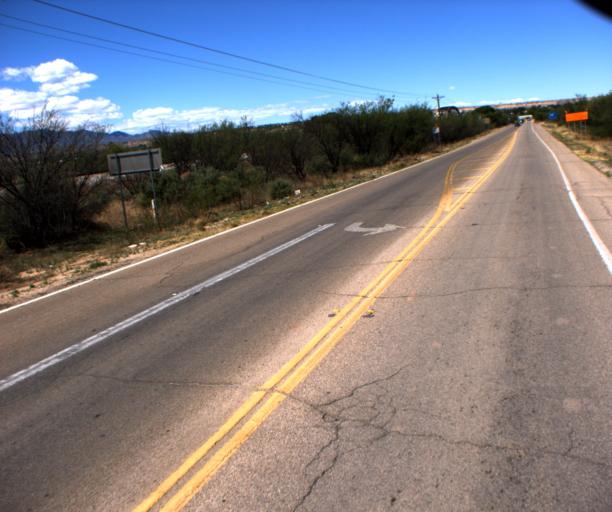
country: US
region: Arizona
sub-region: Cochise County
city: Benson
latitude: 31.9650
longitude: -110.2745
